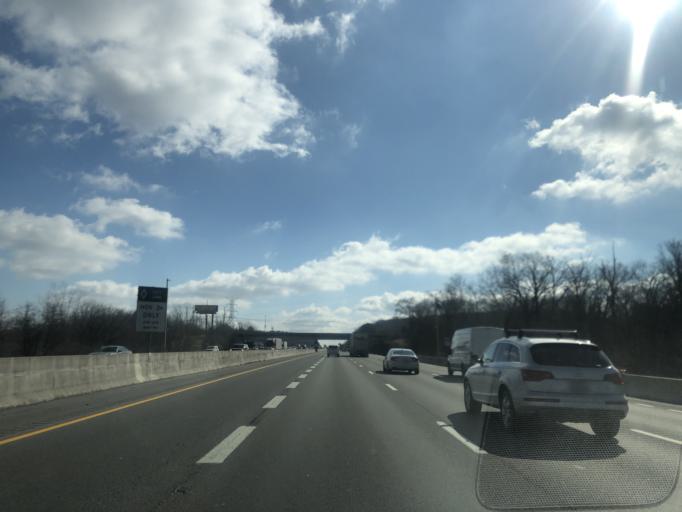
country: US
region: Tennessee
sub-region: Rutherford County
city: La Vergne
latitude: 36.0333
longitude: -86.6418
